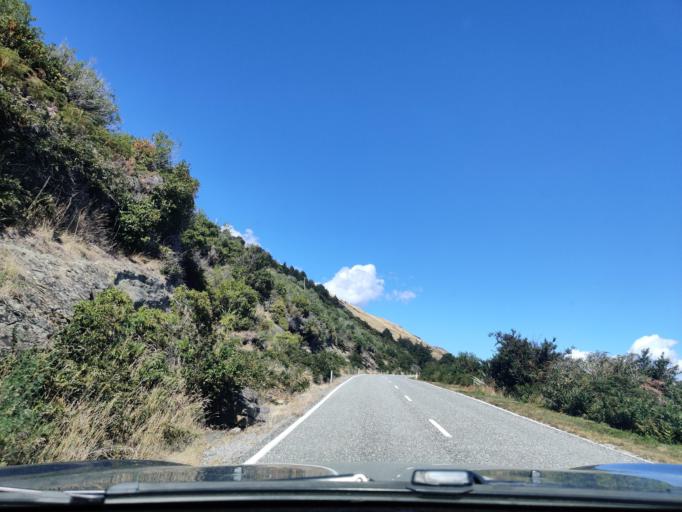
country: NZ
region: Otago
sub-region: Queenstown-Lakes District
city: Queenstown
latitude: -44.9519
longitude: 168.4368
